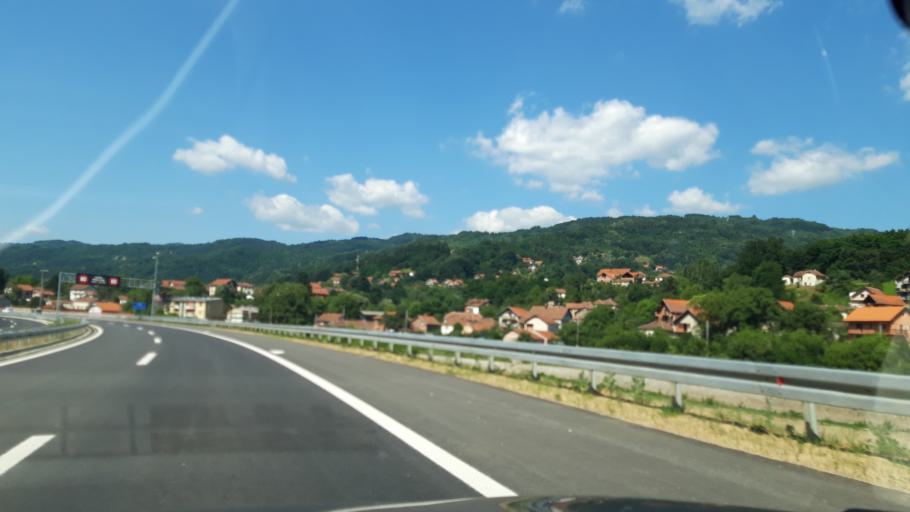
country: RS
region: Central Serbia
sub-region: Pcinjski Okrug
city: Vladicin Han
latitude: 42.8261
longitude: 22.1287
